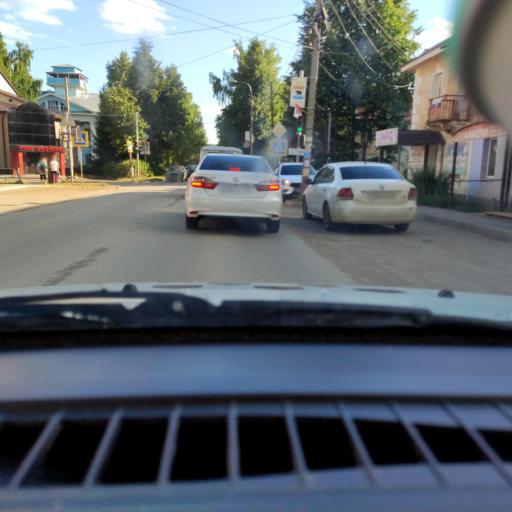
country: RU
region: Perm
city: Ocher
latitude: 57.8833
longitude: 54.7147
